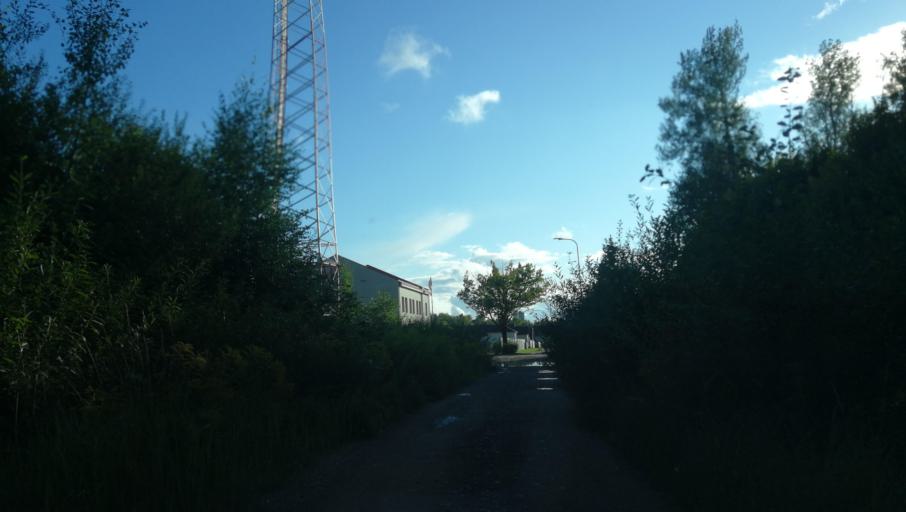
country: LV
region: Valmieras Rajons
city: Valmiera
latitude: 57.5293
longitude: 25.4634
